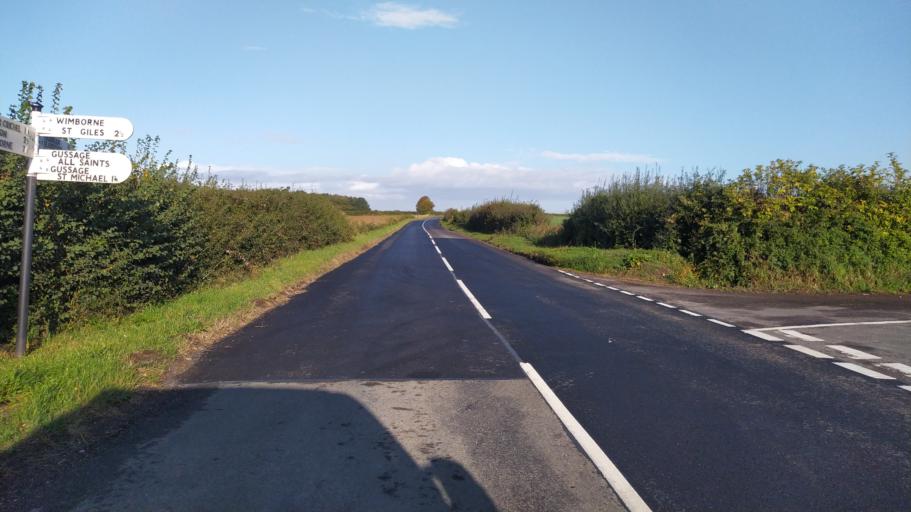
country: GB
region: England
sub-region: Dorset
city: Wimborne Minster
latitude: 50.8862
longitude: -1.9987
